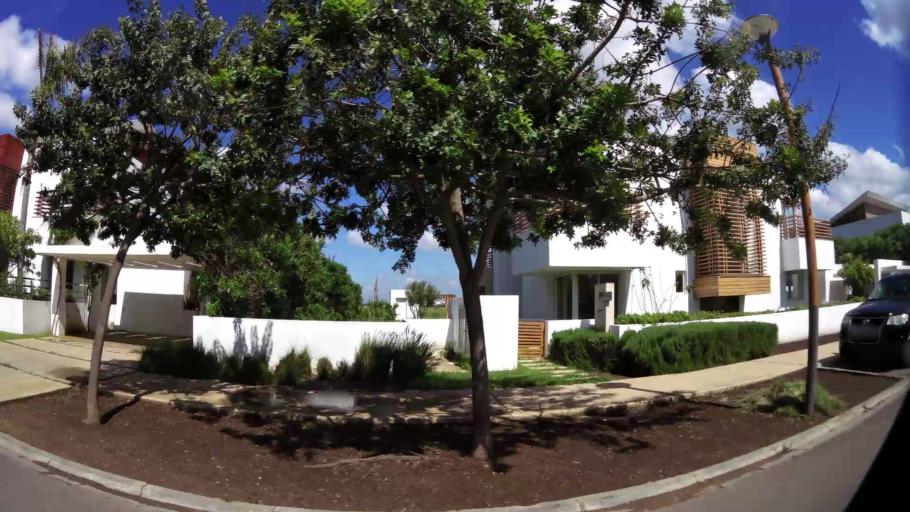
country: MA
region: Grand Casablanca
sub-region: Nouaceur
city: Bouskoura
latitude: 33.4892
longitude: -7.5998
